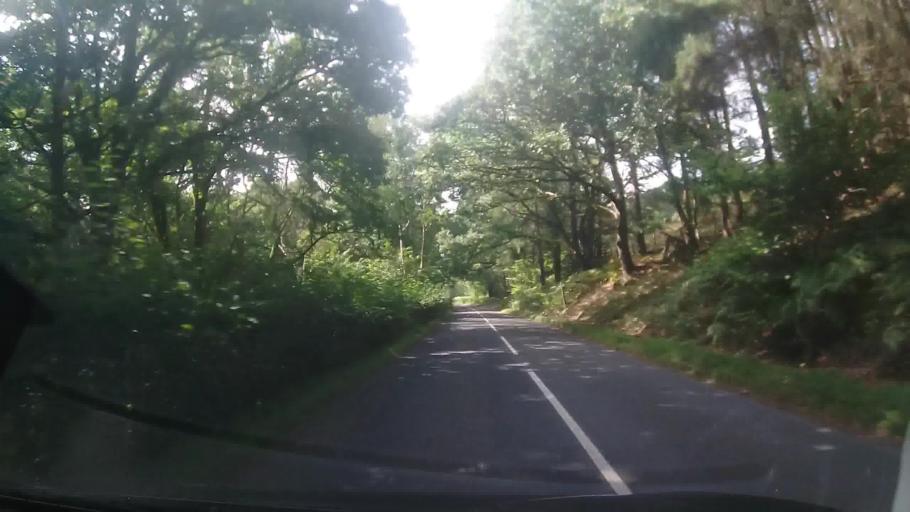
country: GB
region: Wales
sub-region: Sir Powys
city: Rhayader
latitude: 52.2822
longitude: -3.5521
